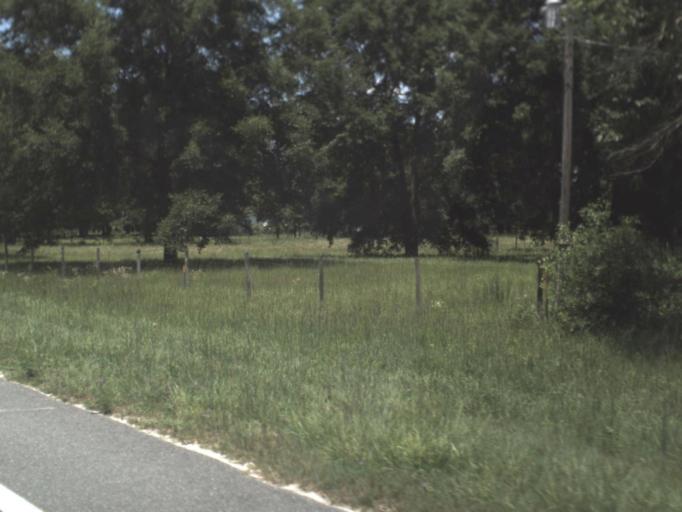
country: US
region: Florida
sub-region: Dixie County
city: Cross City
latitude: 29.8224
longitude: -82.9685
